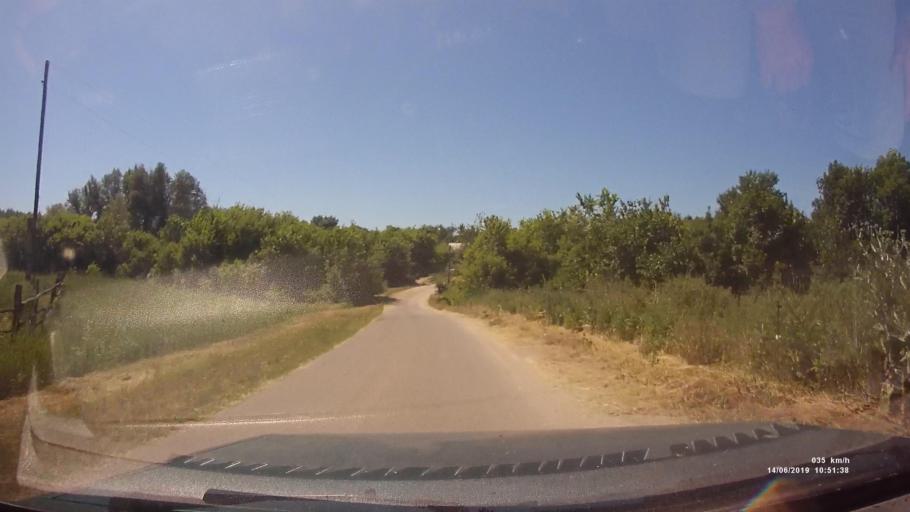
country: RU
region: Rostov
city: Kazanskaya
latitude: 49.8688
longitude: 41.3923
